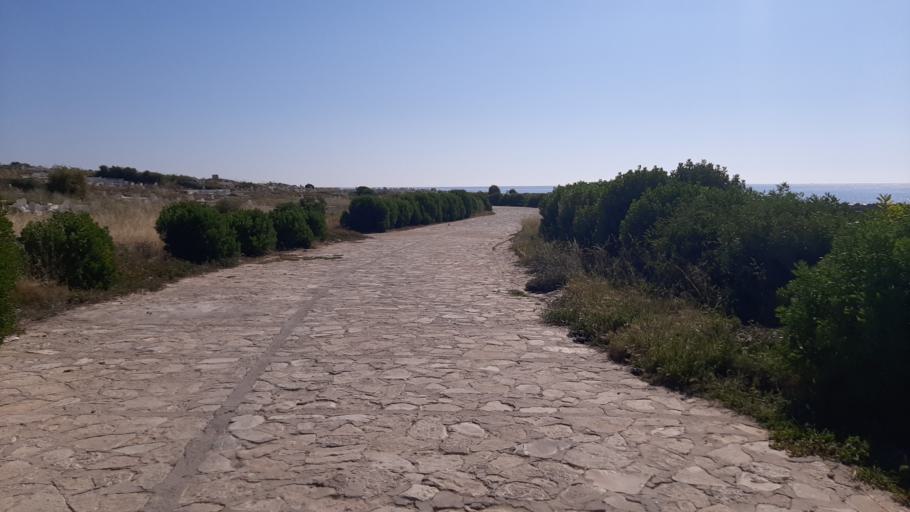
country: TN
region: Al Mahdiyah
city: Mahdia
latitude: 35.5062
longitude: 11.0783
